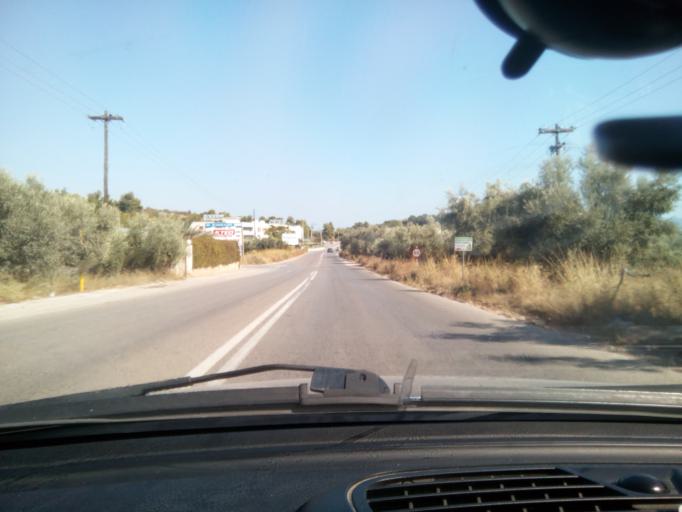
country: GR
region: Central Greece
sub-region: Nomos Evvoias
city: Vasilikon
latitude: 38.4179
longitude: 23.6910
